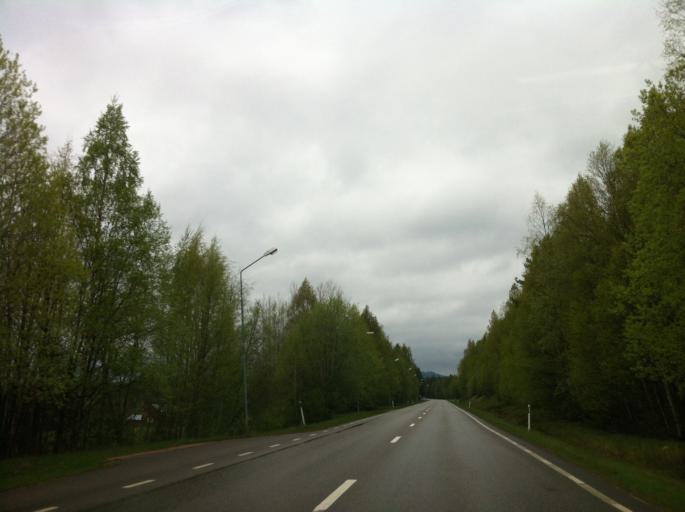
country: SE
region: Jaemtland
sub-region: Harjedalens Kommun
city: Sveg
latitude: 62.0664
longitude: 14.2731
